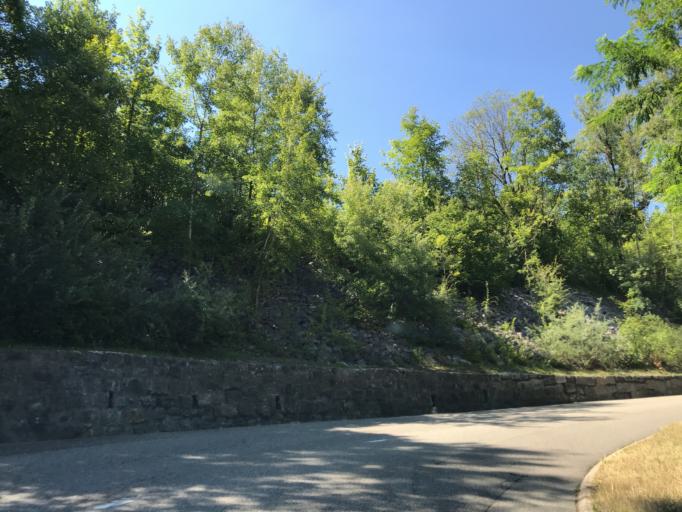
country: FR
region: Rhone-Alpes
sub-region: Departement de la Haute-Savoie
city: Villaz
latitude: 45.9272
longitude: 6.1785
